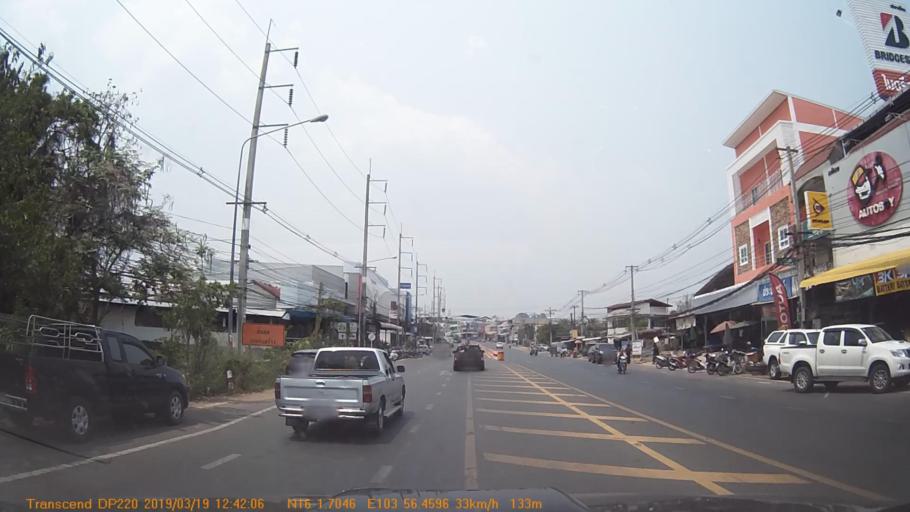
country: TH
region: Roi Et
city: Selaphum
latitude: 16.0285
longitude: 103.9409
